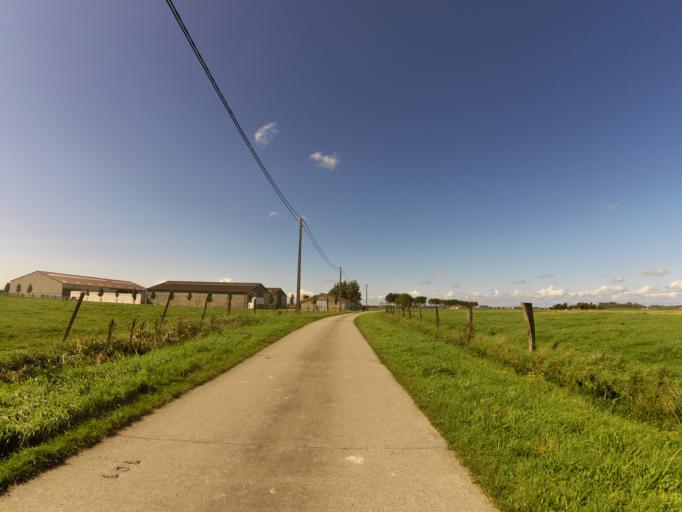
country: BE
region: Flanders
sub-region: Provincie West-Vlaanderen
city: Middelkerke
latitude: 51.1446
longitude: 2.8691
